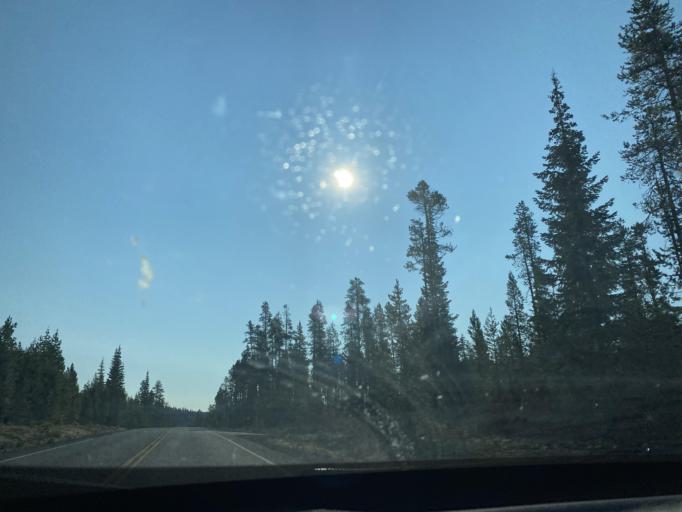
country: US
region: Oregon
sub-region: Deschutes County
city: La Pine
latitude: 43.7041
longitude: -121.3109
